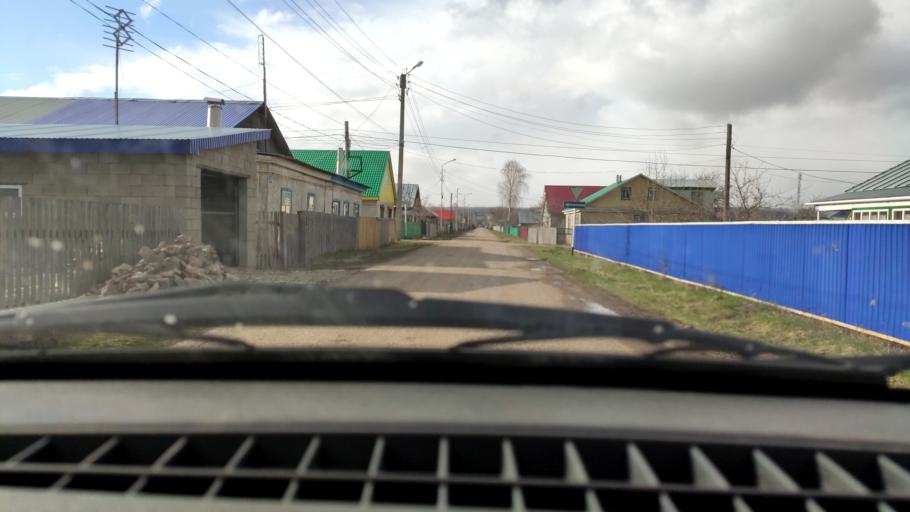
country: RU
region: Bashkortostan
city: Chekmagush
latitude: 55.1460
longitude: 54.6434
